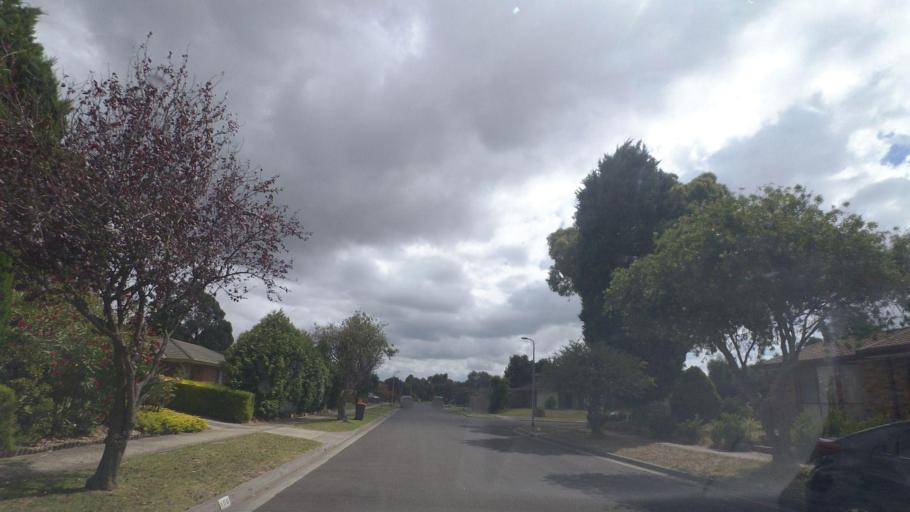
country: AU
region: Victoria
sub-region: Knox
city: Rowville
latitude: -37.9236
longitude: 145.2286
